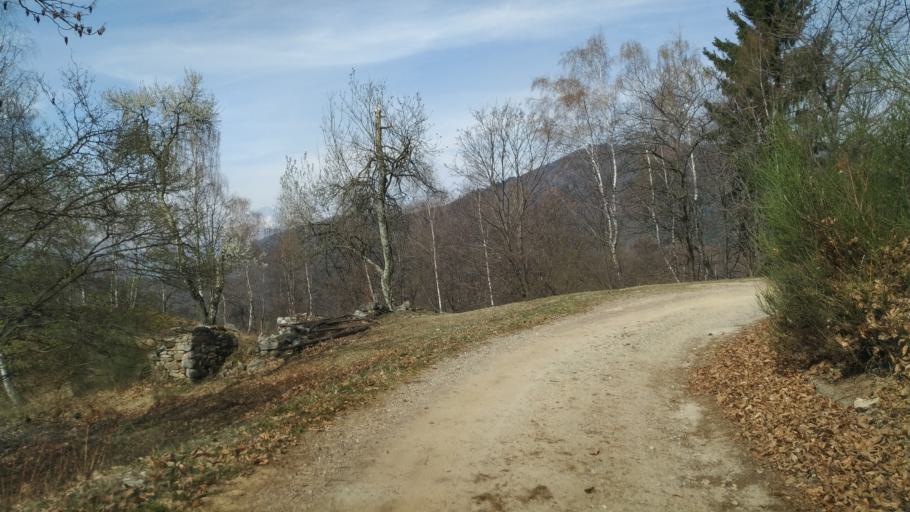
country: IT
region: Piedmont
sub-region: Provincia di Vercelli
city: Civiasco
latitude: 45.8050
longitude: 8.3139
